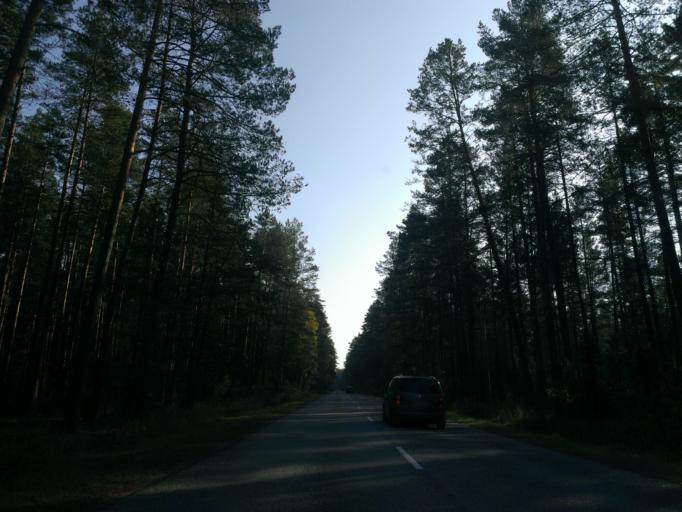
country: LV
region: Garkalne
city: Garkalne
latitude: 57.0210
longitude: 24.4369
